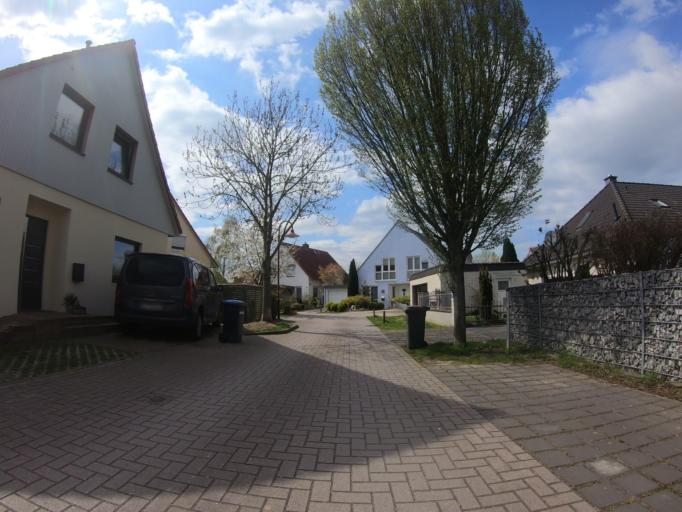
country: DE
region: Lower Saxony
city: Sarstedt
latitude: 52.2385
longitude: 9.8184
